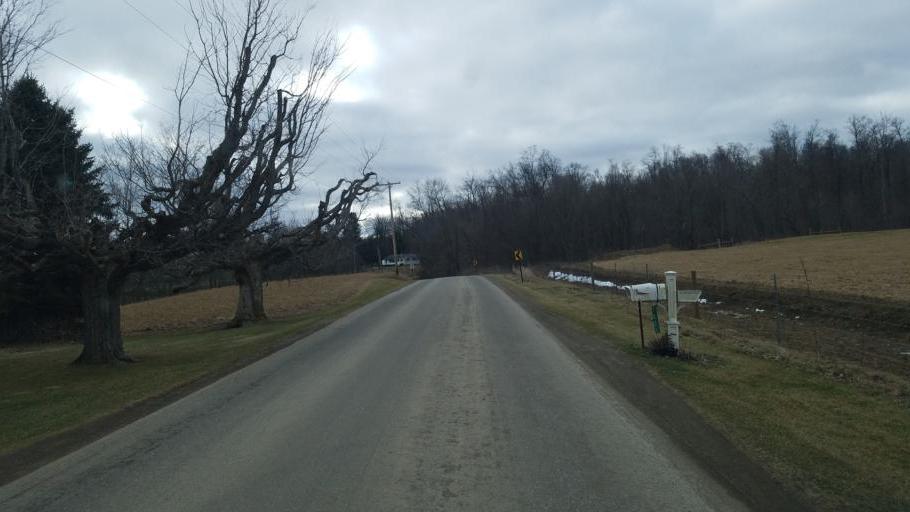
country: US
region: Ohio
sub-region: Morrow County
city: Mount Gilead
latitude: 40.5540
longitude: -82.6777
